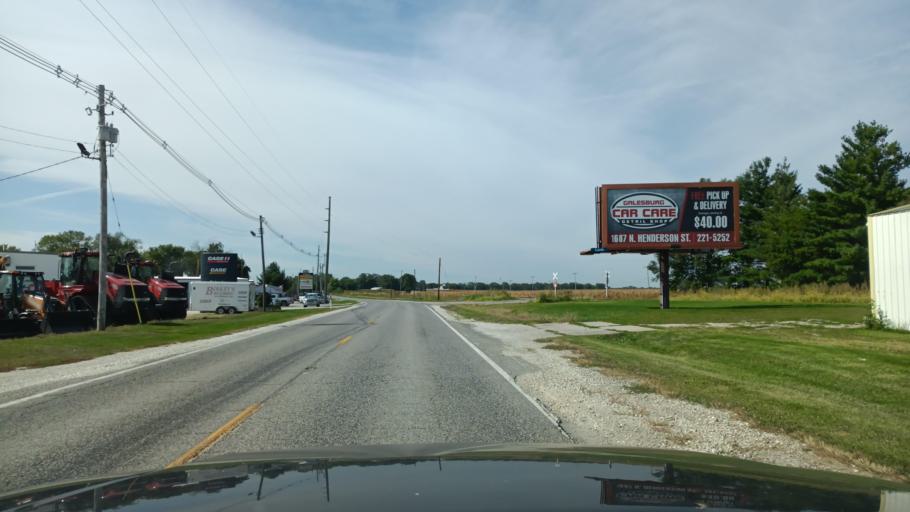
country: US
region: Illinois
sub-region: Knox County
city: Knoxville
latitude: 40.9211
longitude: -90.3141
